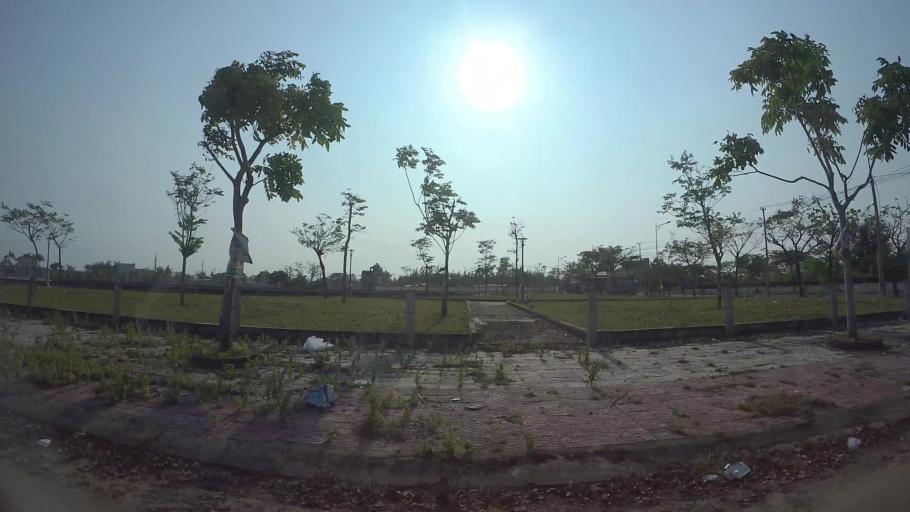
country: VN
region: Da Nang
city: Ngu Hanh Son
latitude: 15.9609
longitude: 108.2586
